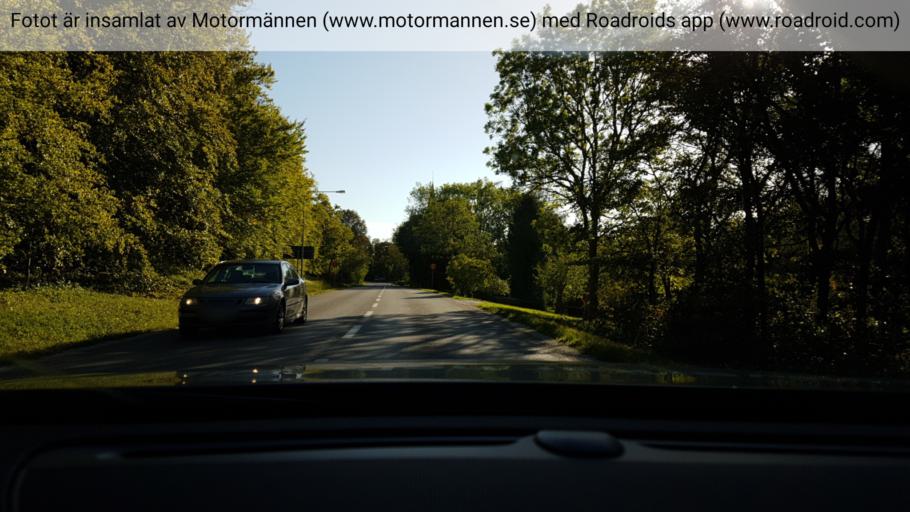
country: SE
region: Gotland
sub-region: Gotland
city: Klintehamn
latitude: 57.3815
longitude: 18.2353
